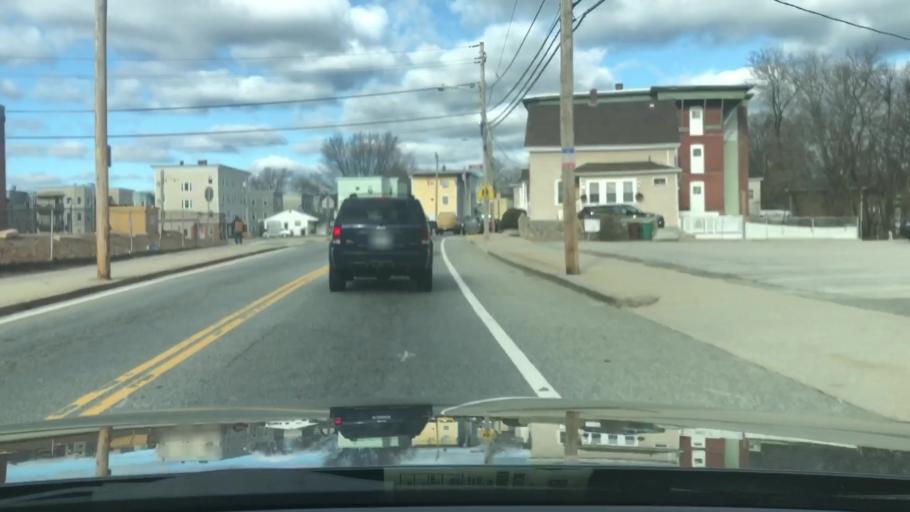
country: US
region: Rhode Island
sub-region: Providence County
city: Woonsocket
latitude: 42.0126
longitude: -71.5013
